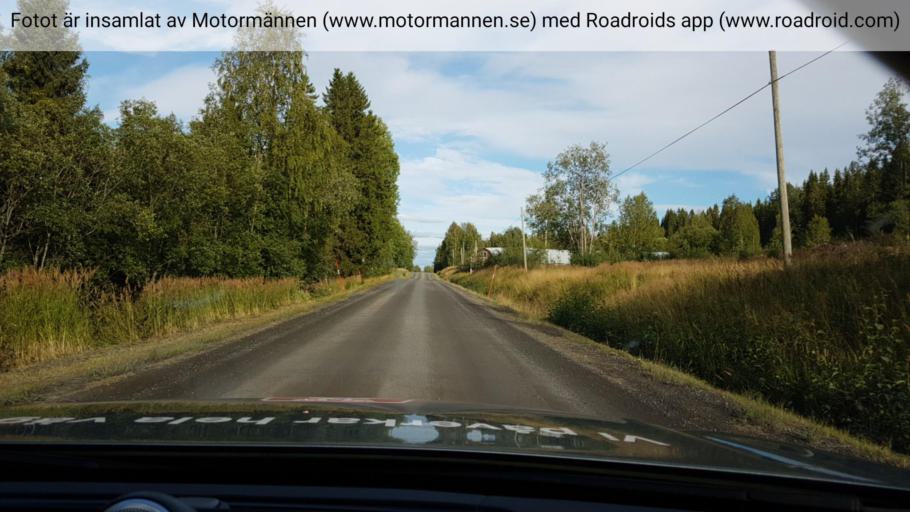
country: SE
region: Jaemtland
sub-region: Stroemsunds Kommun
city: Stroemsund
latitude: 64.1422
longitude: 15.7219
